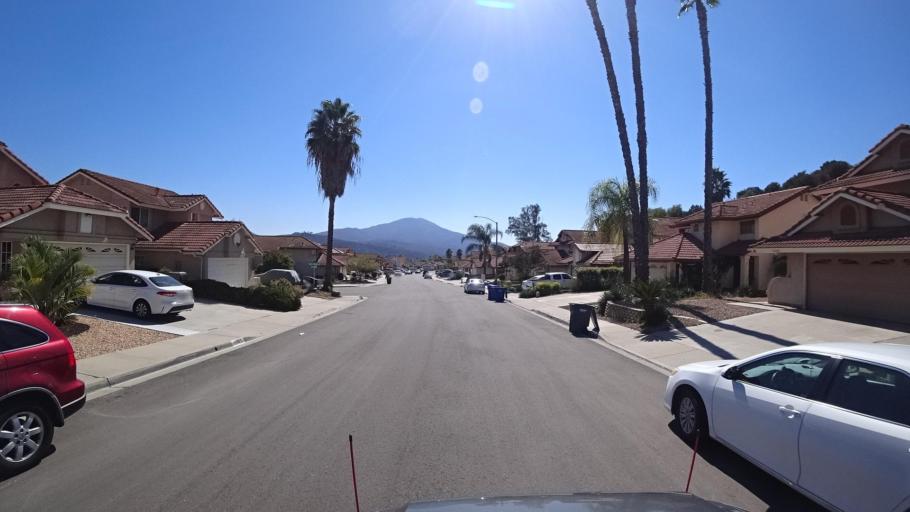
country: US
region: California
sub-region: San Diego County
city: Rancho San Diego
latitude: 32.7527
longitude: -116.9358
